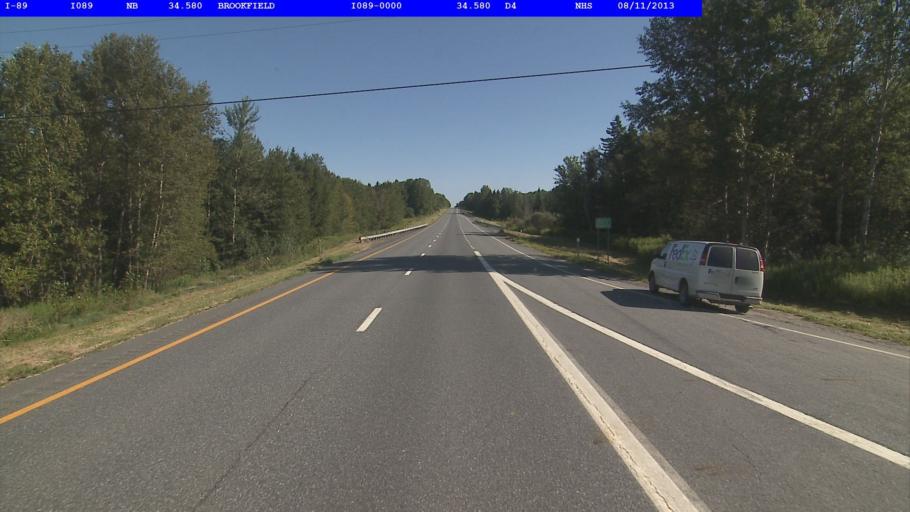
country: US
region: Vermont
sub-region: Orange County
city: Randolph
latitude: 43.9974
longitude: -72.6231
